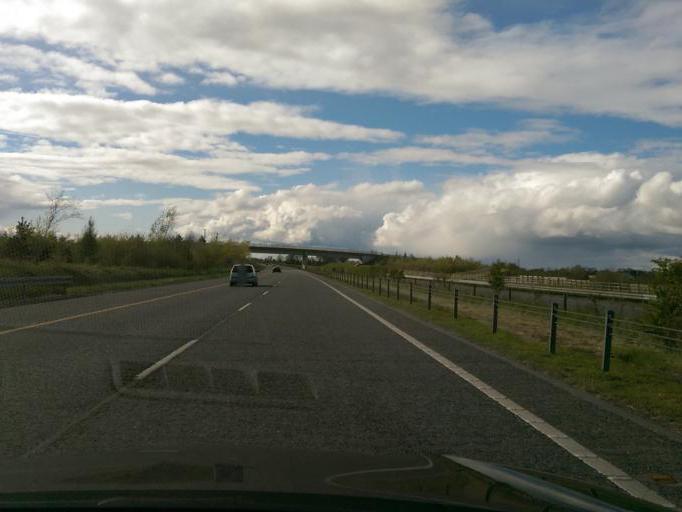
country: IE
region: Leinster
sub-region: An Mhi
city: Longwood
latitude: 53.4334
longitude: -6.9982
